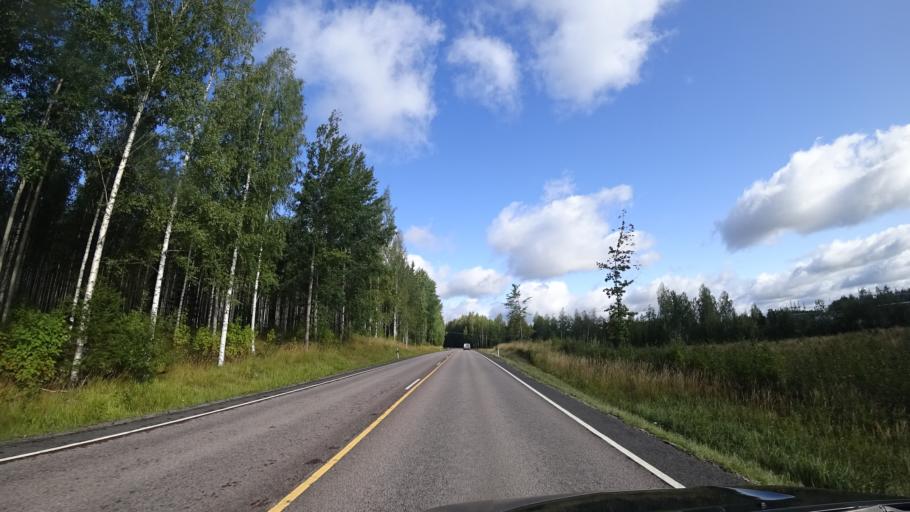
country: FI
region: Uusimaa
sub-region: Helsinki
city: Tuusula
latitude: 60.4914
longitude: 24.9389
